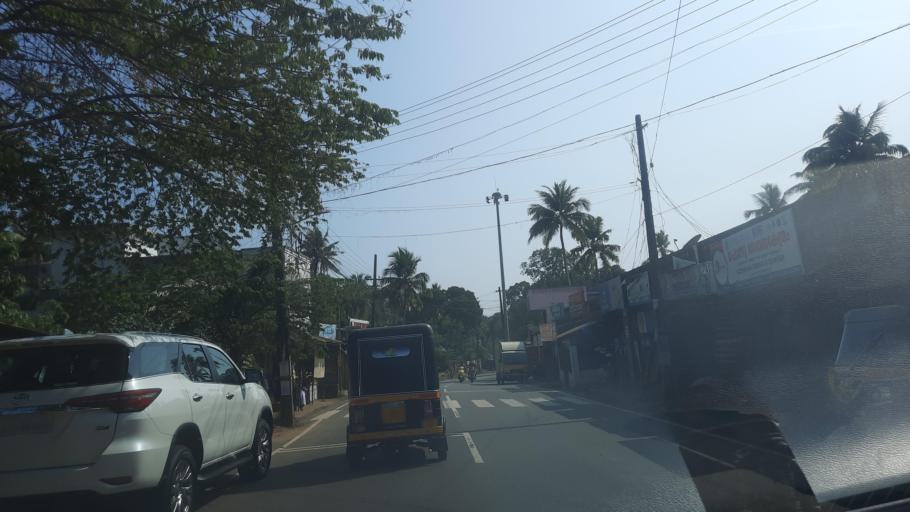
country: IN
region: Kerala
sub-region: Thiruvananthapuram
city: Nedumangad
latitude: 8.5733
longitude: 76.9255
